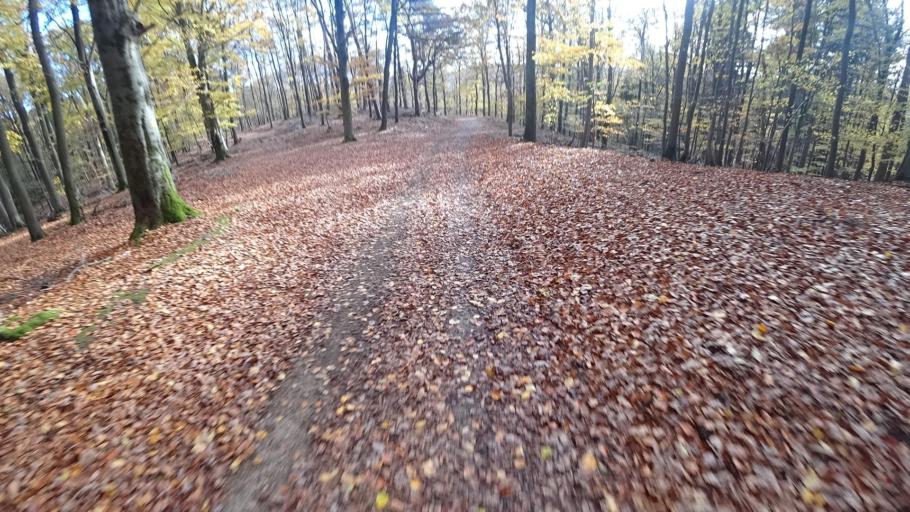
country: DE
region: Rheinland-Pfalz
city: Lind
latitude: 50.4854
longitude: 6.9457
